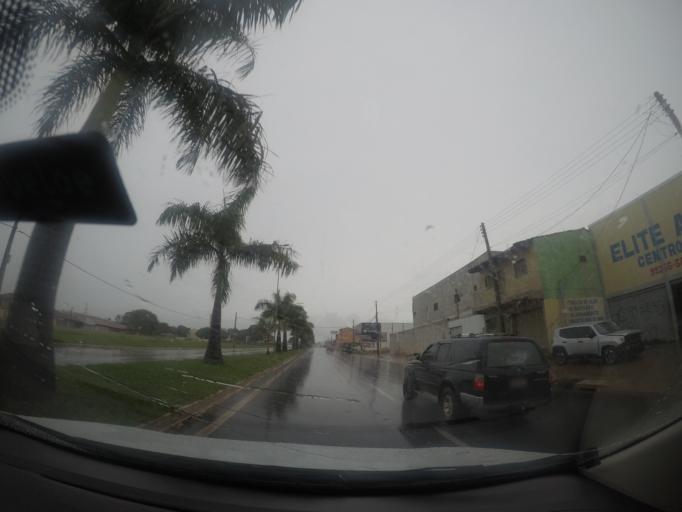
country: BR
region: Goias
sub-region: Goiania
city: Goiania
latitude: -16.6428
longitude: -49.3146
